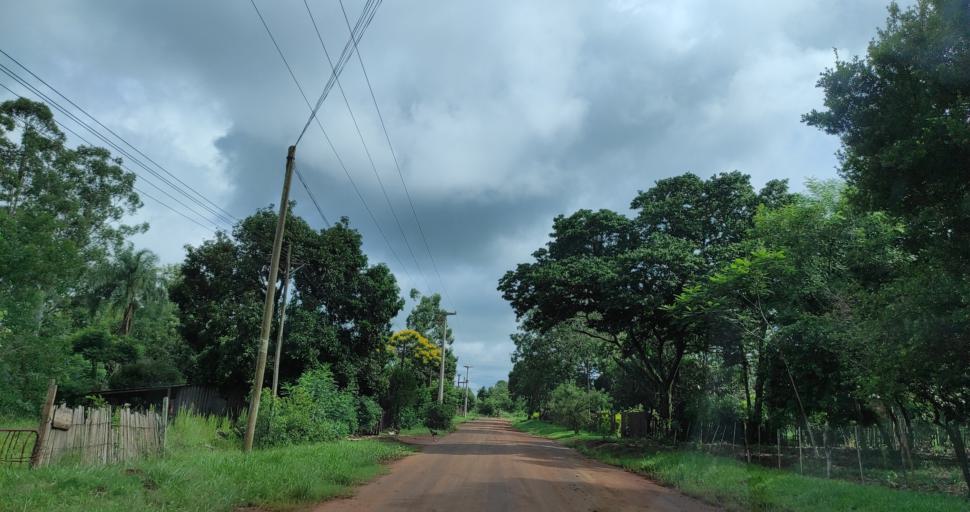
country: AR
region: Corrientes
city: San Carlos
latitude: -27.7475
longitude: -55.8916
